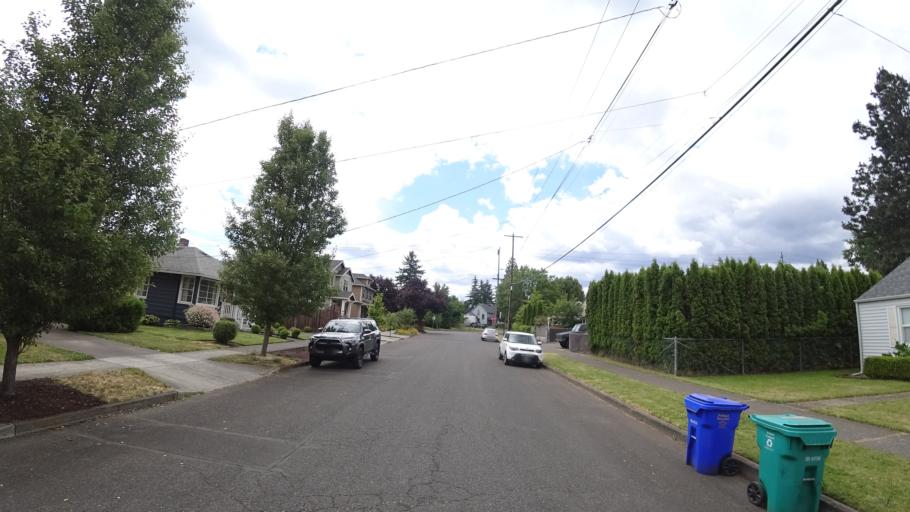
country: US
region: Oregon
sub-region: Multnomah County
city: Portland
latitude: 45.5872
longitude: -122.7242
